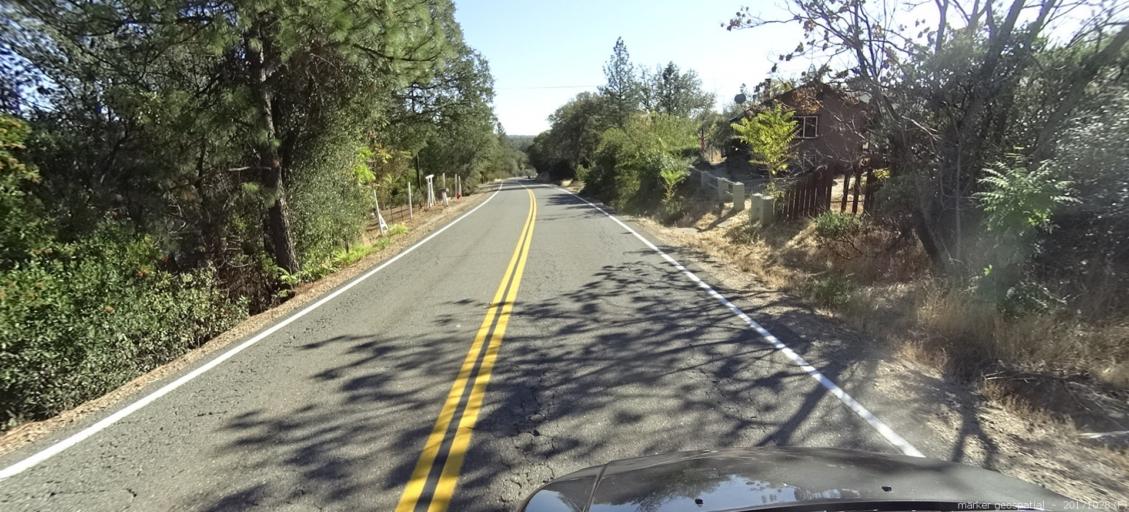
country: US
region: California
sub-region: Shasta County
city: Shasta
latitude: 40.6176
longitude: -122.4623
